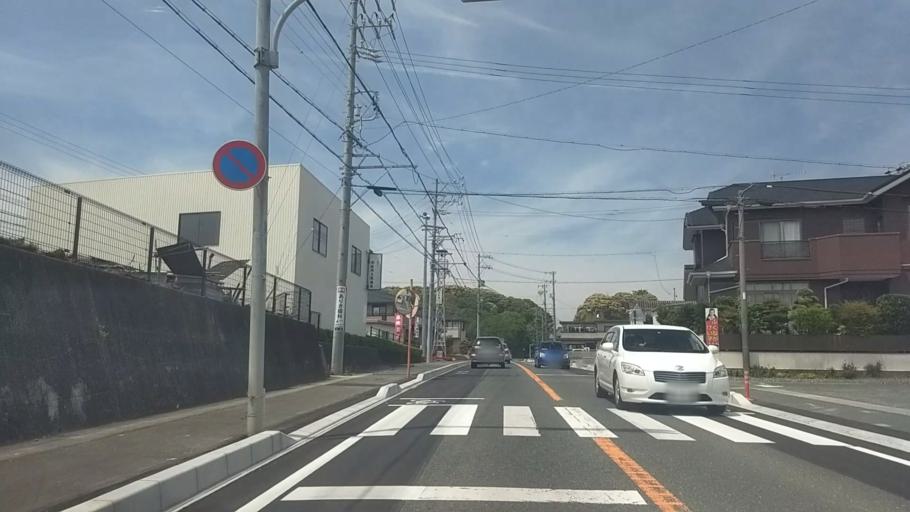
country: JP
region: Shizuoka
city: Kosai-shi
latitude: 34.7424
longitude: 137.5151
